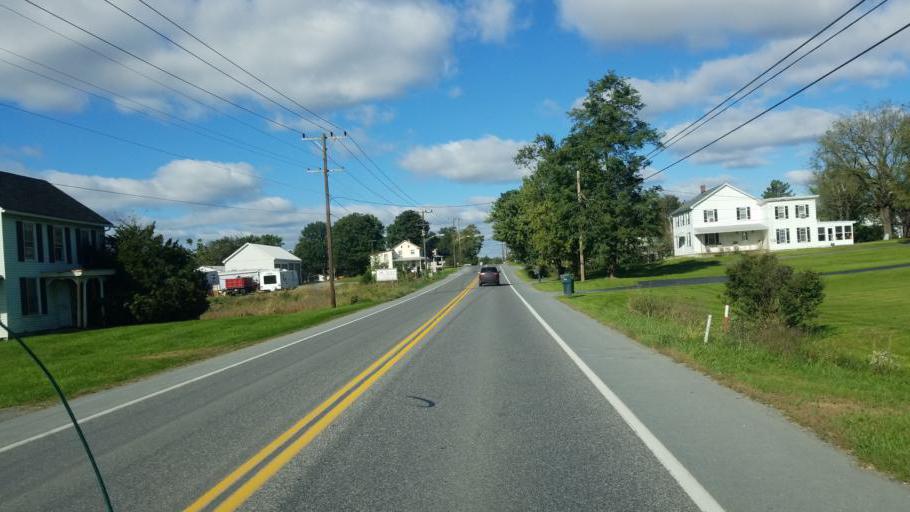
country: US
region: Pennsylvania
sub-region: Franklin County
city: Greencastle
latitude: 39.8038
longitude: -77.8014
